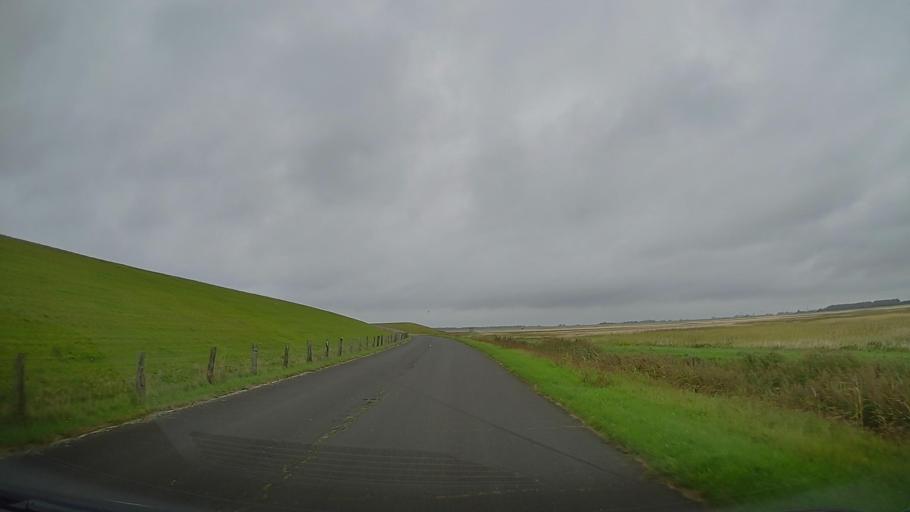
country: DE
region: Schleswig-Holstein
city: Busenwurth
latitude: 54.0555
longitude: 8.9867
